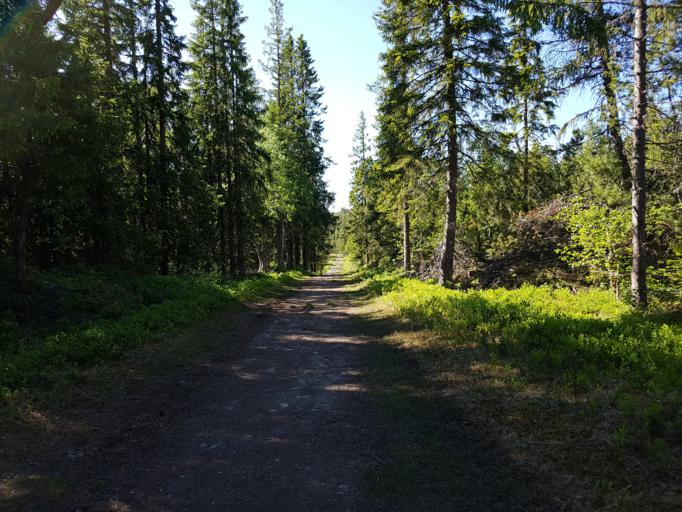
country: NO
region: Sor-Trondelag
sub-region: Trondheim
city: Trondheim
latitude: 63.4276
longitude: 10.2958
